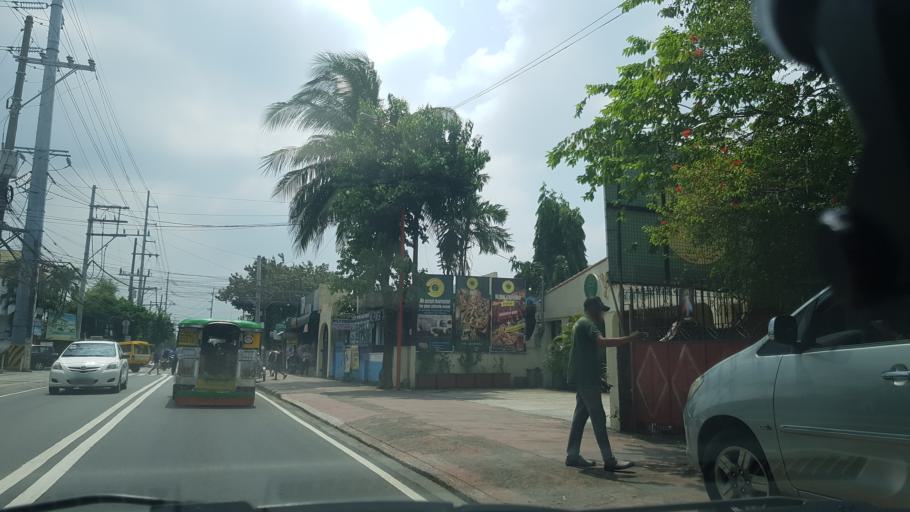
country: PH
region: Calabarzon
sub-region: Province of Rizal
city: Antipolo
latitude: 14.6387
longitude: 121.1217
